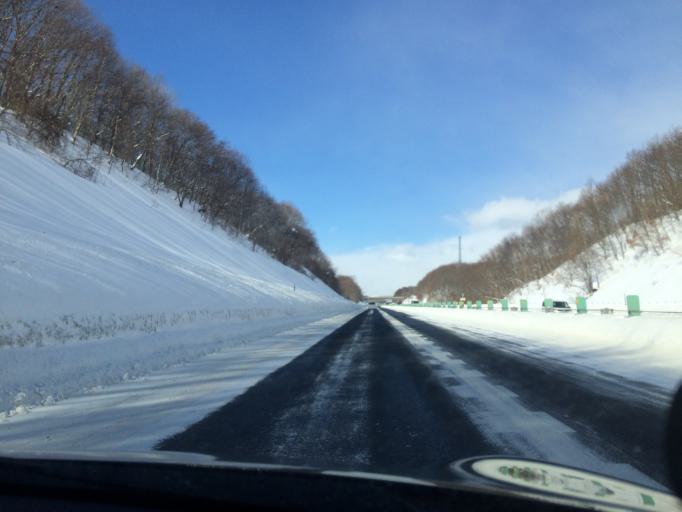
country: JP
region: Hokkaido
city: Kitahiroshima
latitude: 42.9287
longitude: 141.5348
